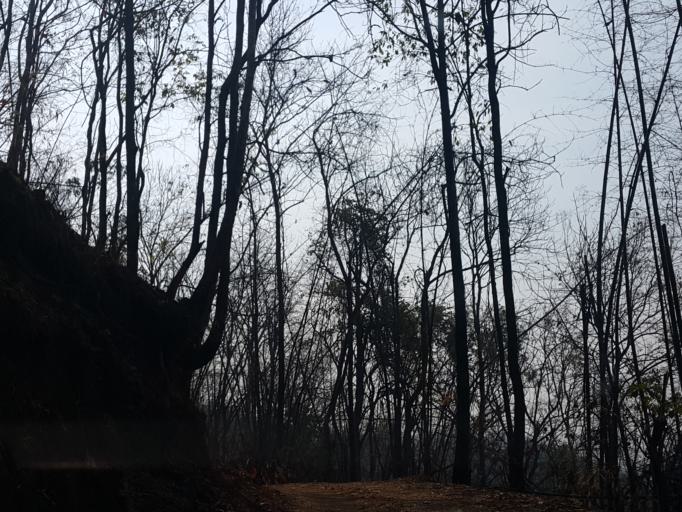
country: TH
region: Chiang Mai
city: Hang Dong
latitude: 18.7523
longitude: 98.8532
